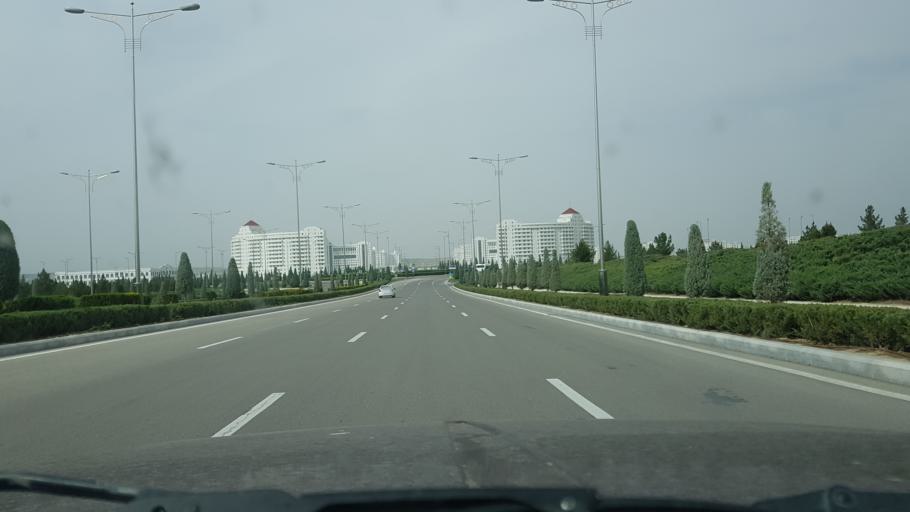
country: TM
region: Ahal
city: Ashgabat
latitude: 37.8863
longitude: 58.3338
